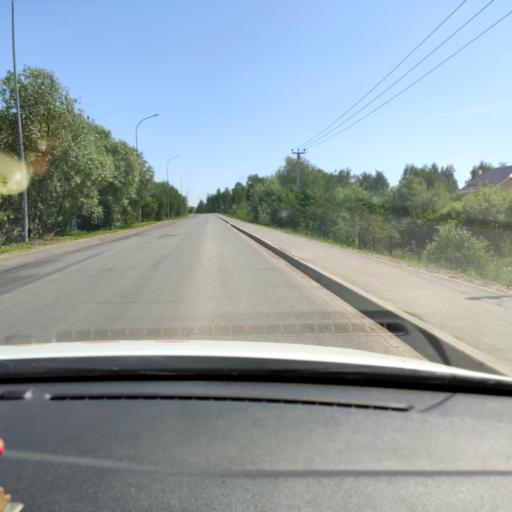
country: RU
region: Tatarstan
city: Stolbishchi
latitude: 55.6957
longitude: 49.1967
